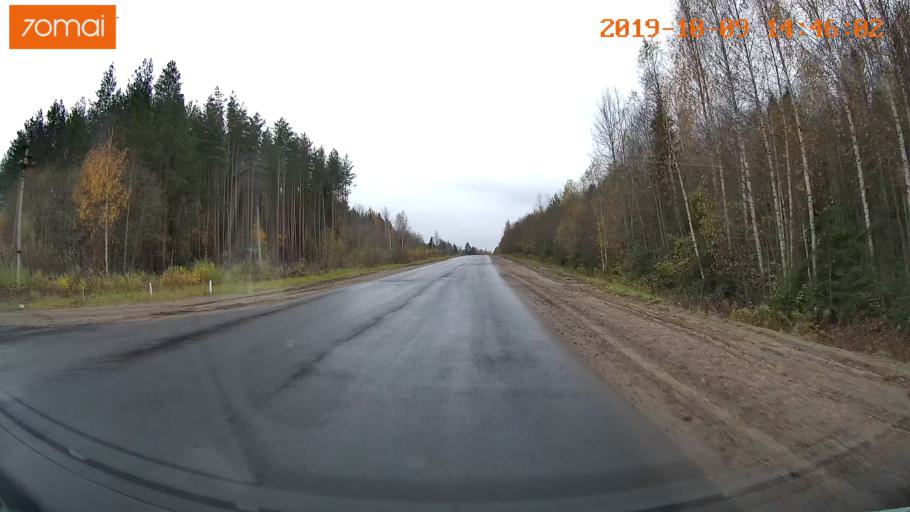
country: RU
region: Kostroma
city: Buy
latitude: 58.4364
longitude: 41.5772
